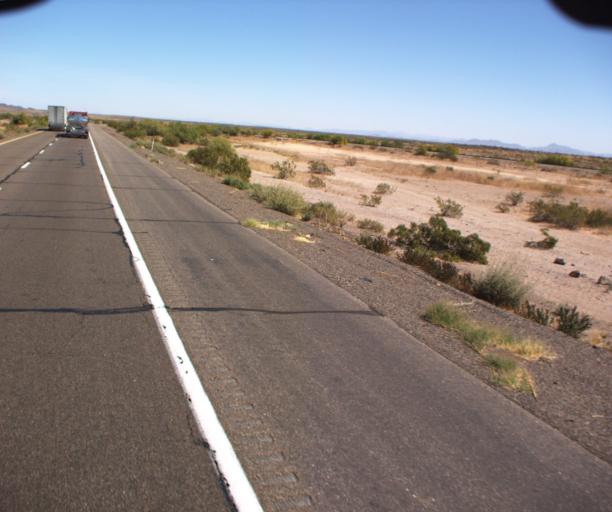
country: US
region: Arizona
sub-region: Maricopa County
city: Gila Bend
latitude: 32.8768
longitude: -113.1175
